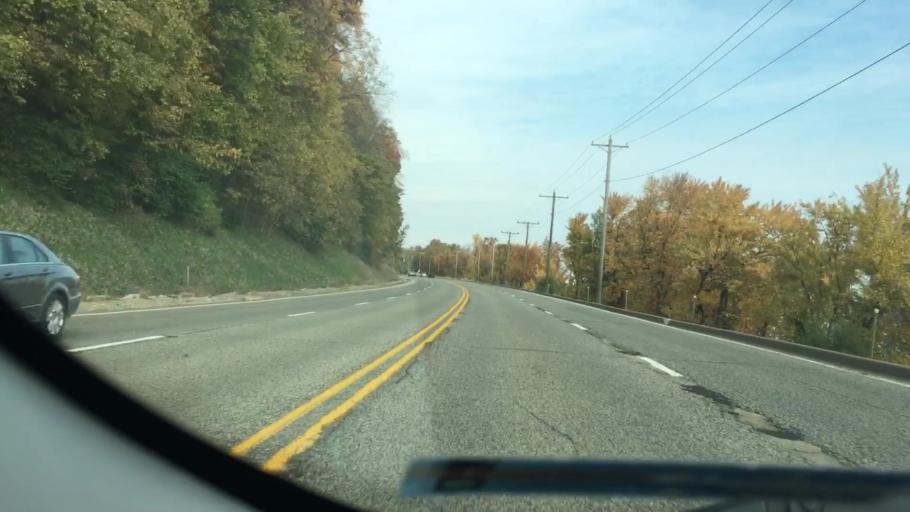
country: US
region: Illinois
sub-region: Peoria County
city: Peoria Heights
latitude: 40.7340
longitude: -89.5515
